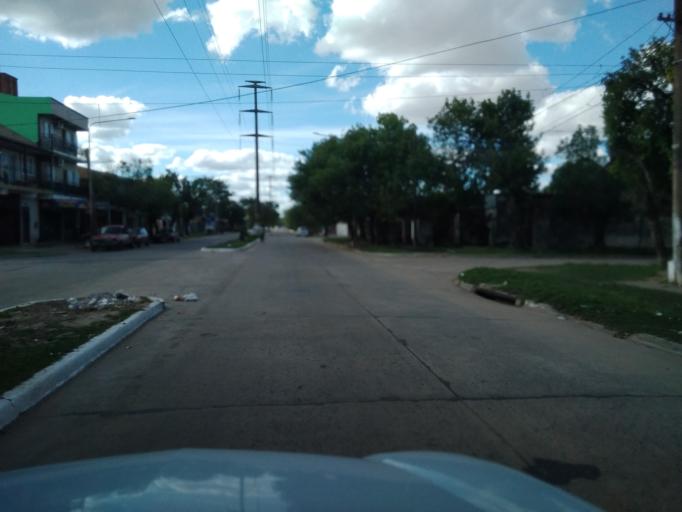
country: AR
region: Corrientes
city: Corrientes
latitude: -27.4966
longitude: -58.8381
